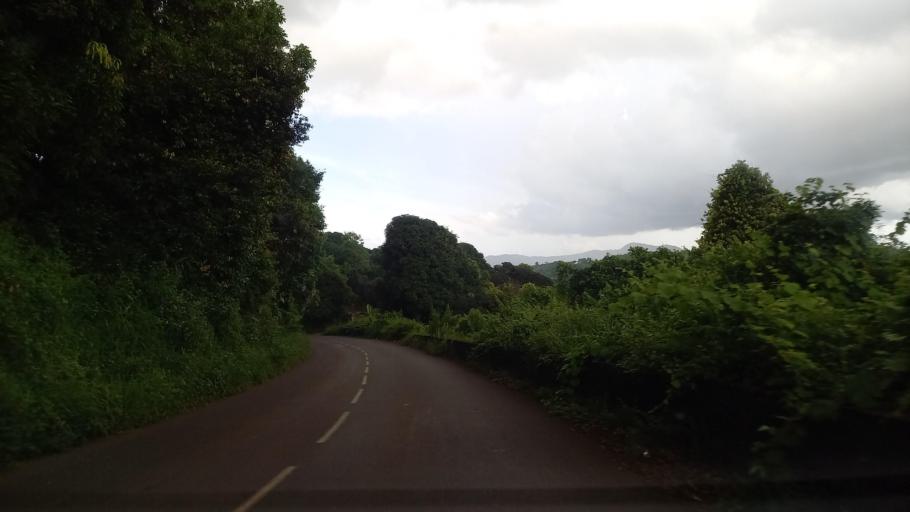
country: YT
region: Tsingoni
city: Tsingoni
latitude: -12.7845
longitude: 45.1486
